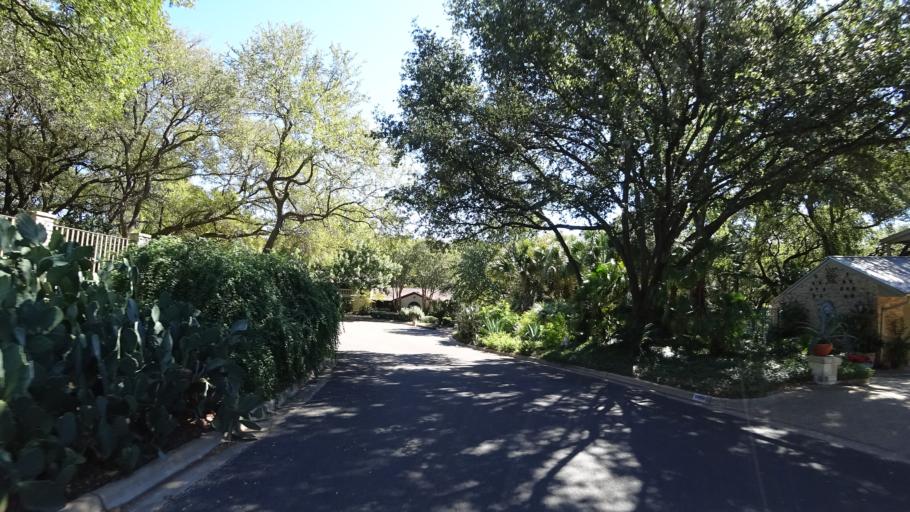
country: US
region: Texas
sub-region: Travis County
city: West Lake Hills
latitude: 30.3127
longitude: -97.7683
